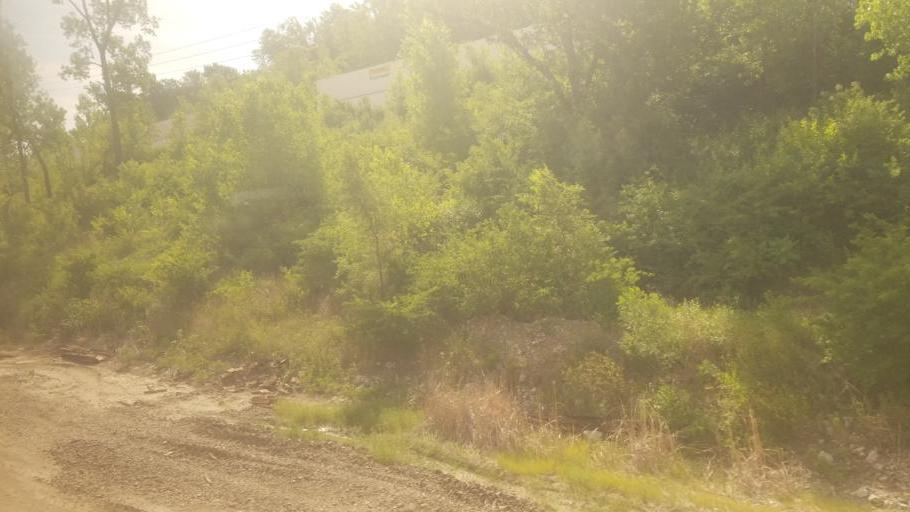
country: US
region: Kansas
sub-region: Wyandotte County
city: Kansas City
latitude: 39.0796
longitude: -94.6127
